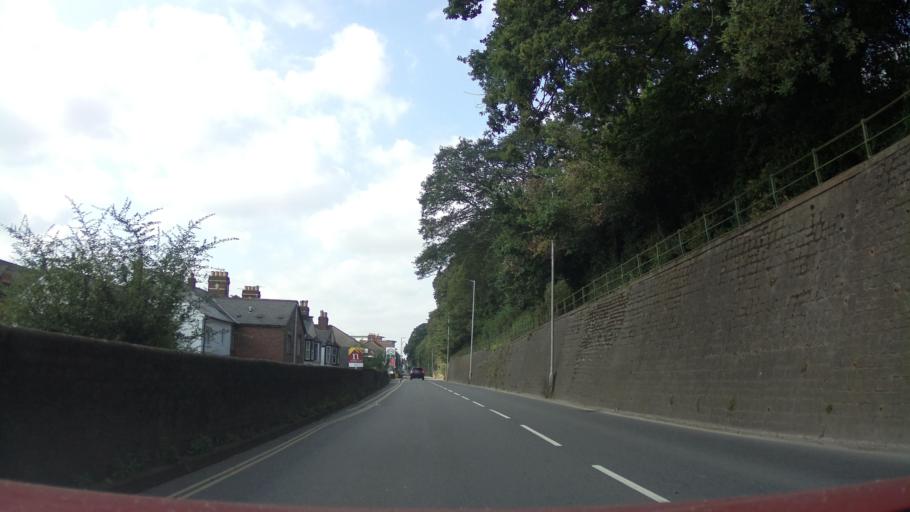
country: GB
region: England
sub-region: Devon
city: Exeter
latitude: 50.7373
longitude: -3.5445
